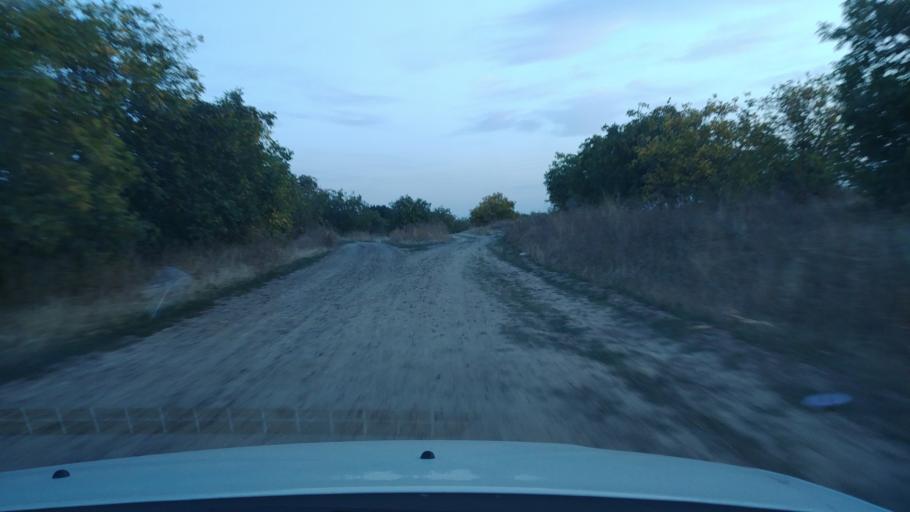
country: MD
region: Rezina
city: Saharna
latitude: 47.6822
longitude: 28.9080
